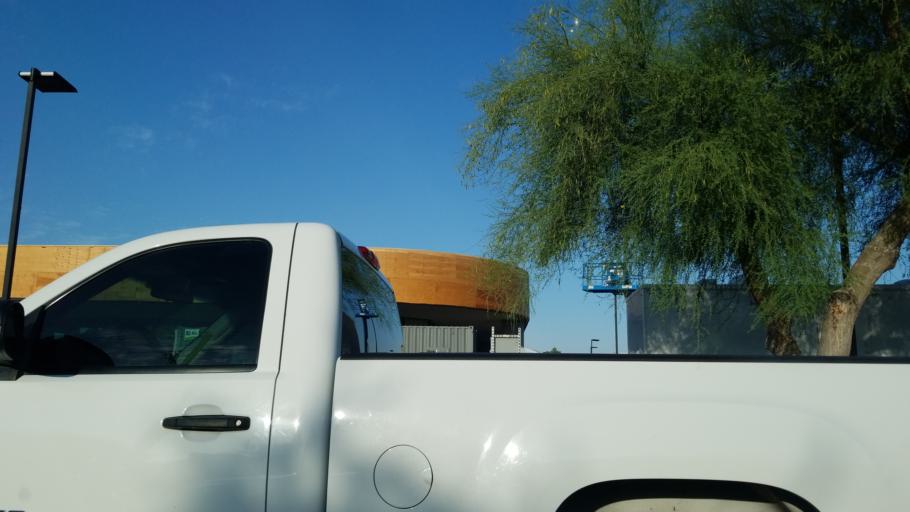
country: US
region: Arizona
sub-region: Maricopa County
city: Glendale
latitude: 33.6392
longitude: -112.0871
